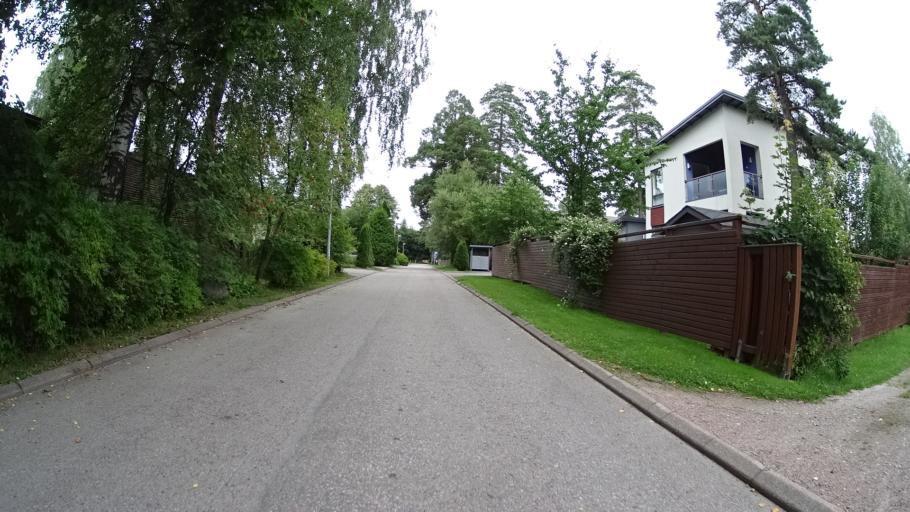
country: FI
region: Uusimaa
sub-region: Helsinki
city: Koukkuniemi
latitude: 60.1668
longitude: 24.7786
